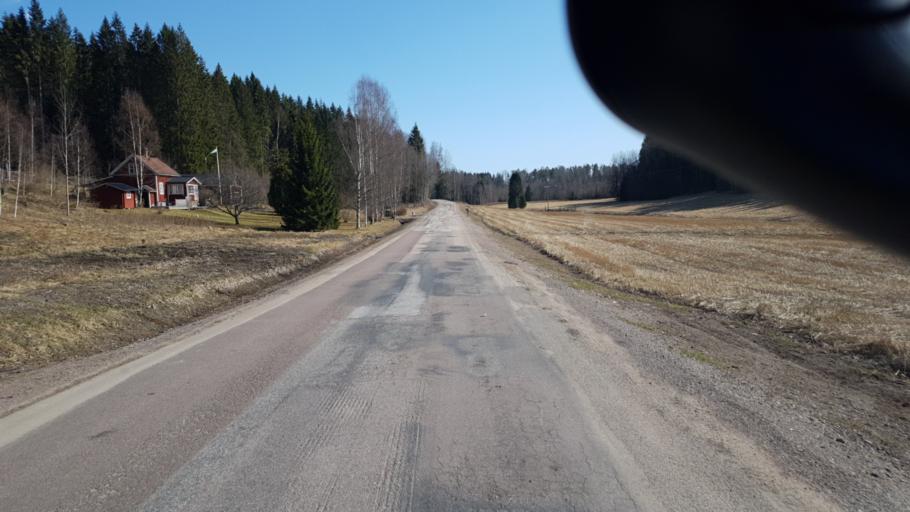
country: SE
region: Vaermland
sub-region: Arvika Kommun
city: Arvika
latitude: 59.6441
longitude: 12.8088
